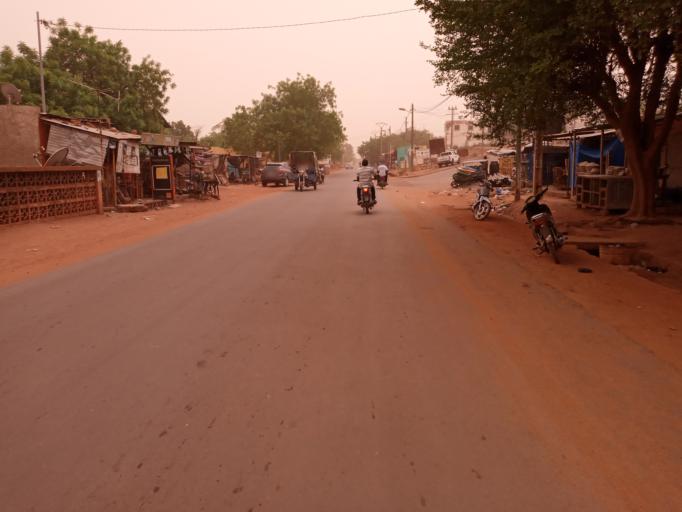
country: ML
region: Koulikoro
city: Koulikoro
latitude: 12.8602
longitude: -7.5591
